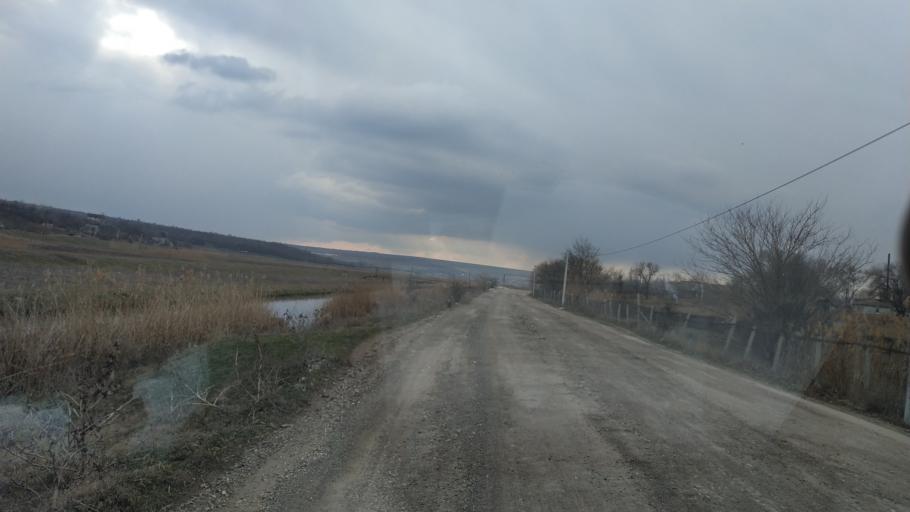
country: MD
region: Anenii Noi
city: Anenii Noi
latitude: 46.8894
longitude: 29.2982
